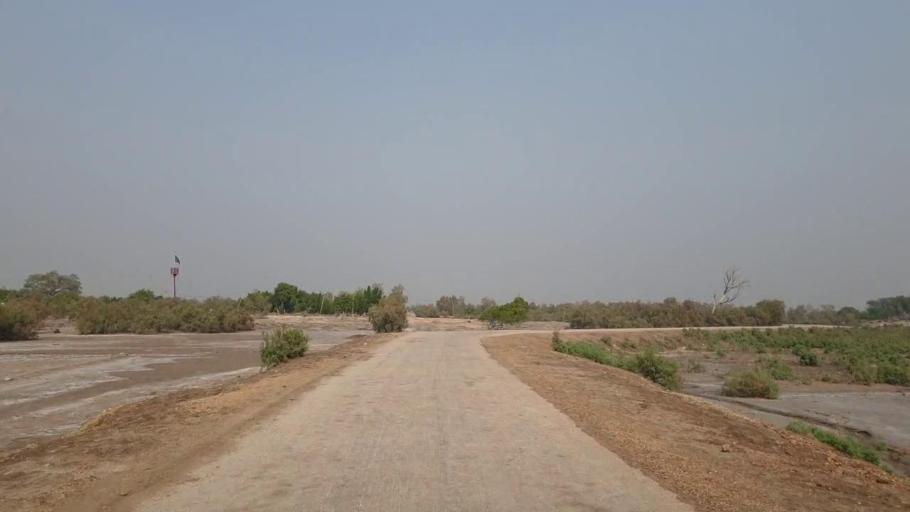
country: PK
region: Sindh
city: Bhan
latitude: 26.4882
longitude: 67.7000
